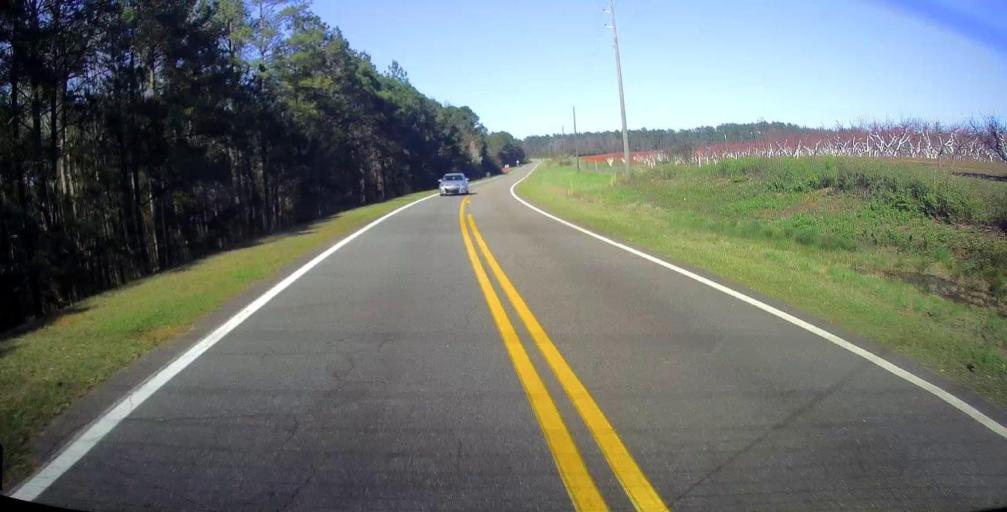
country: US
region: Georgia
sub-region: Peach County
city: Fort Valley
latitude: 32.5973
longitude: -83.9879
